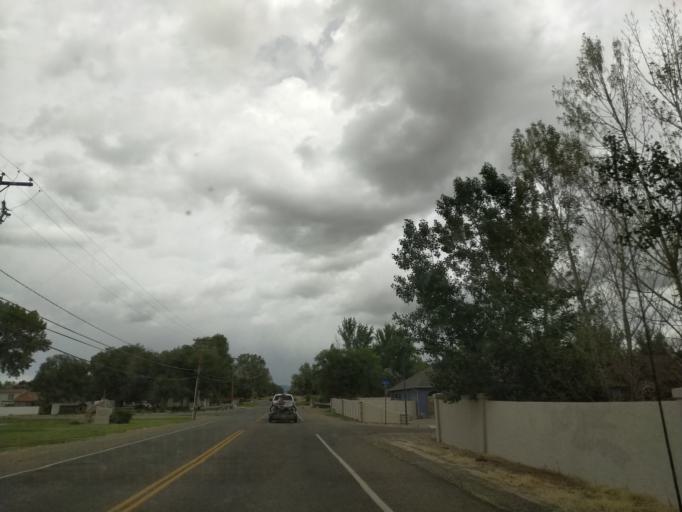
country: US
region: Colorado
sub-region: Mesa County
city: Grand Junction
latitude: 39.0974
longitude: -108.5616
